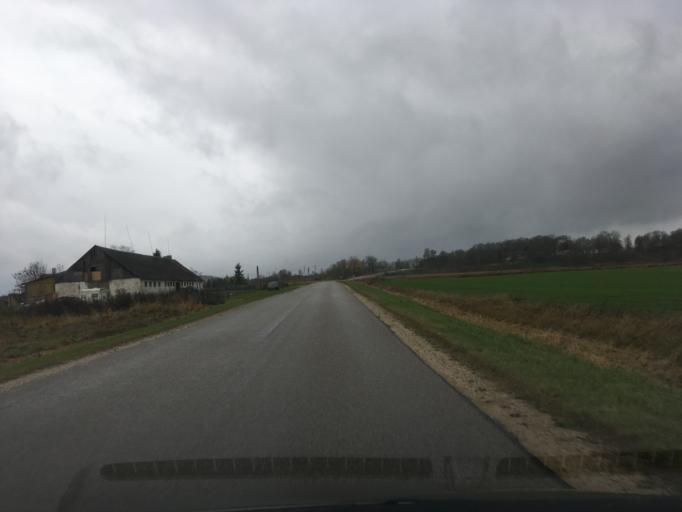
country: EE
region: Laeaene
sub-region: Lihula vald
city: Lihula
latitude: 58.6961
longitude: 23.8506
